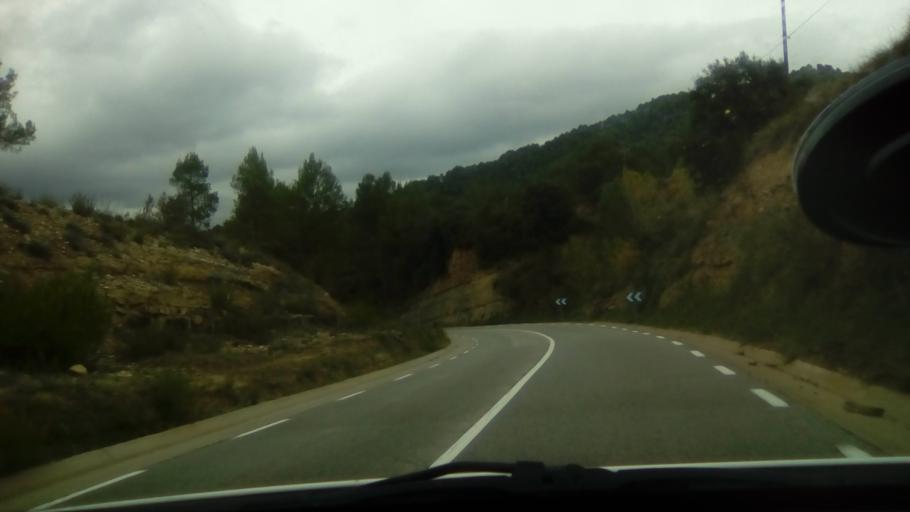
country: ES
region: Catalonia
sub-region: Provincia de Barcelona
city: Manresa
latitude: 41.6884
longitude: 1.8733
